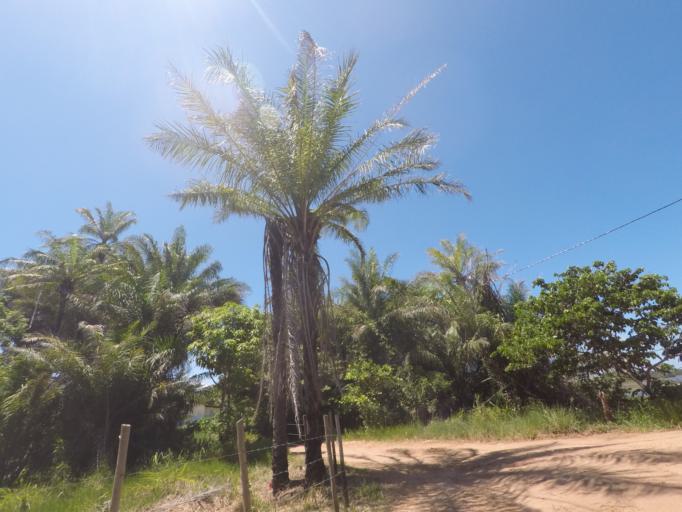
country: BR
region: Bahia
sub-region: Marau
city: Marau
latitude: -14.0255
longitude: -38.9500
